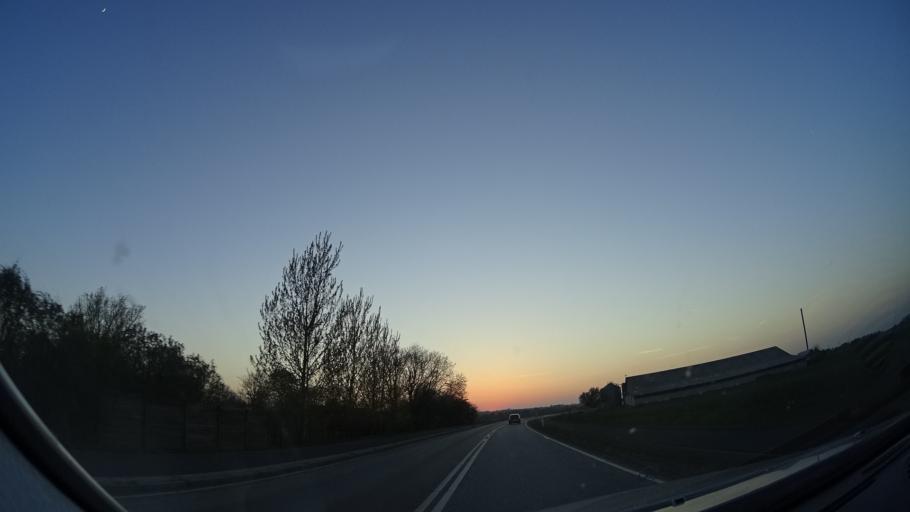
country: DK
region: Zealand
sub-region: Lejre Kommune
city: Ejby
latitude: 55.6585
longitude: 11.9109
